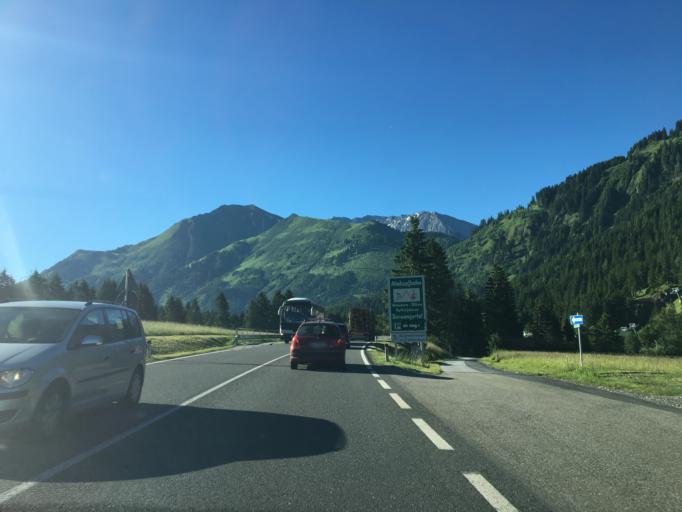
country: AT
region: Tyrol
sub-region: Politischer Bezirk Reutte
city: Bichlbach
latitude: 47.4307
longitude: 10.7758
